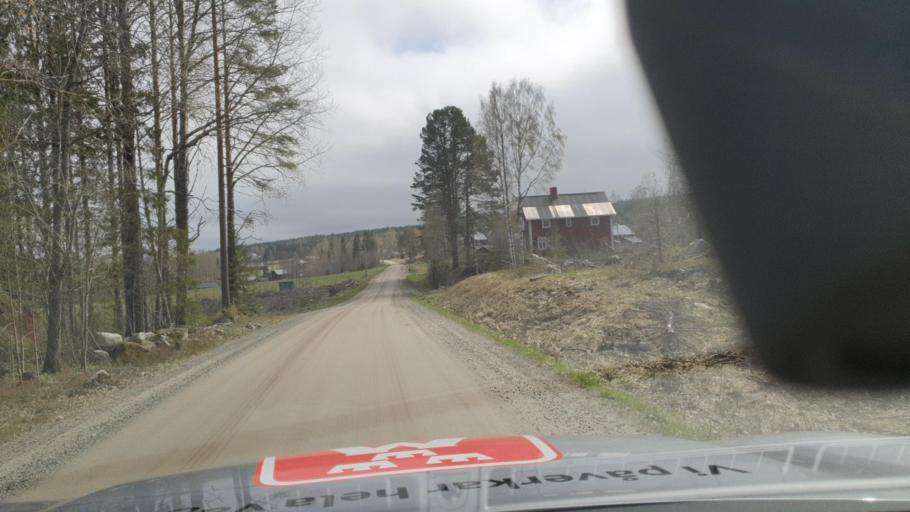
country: SE
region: Vaesterbotten
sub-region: Bjurholms Kommun
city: Bjurholm
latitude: 63.6739
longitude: 18.9961
